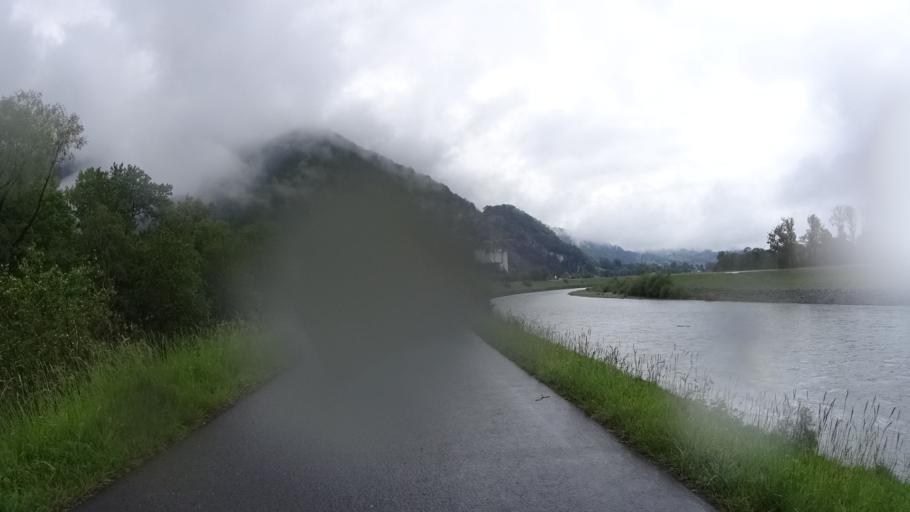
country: LI
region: Balzers
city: Balzers
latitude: 47.0592
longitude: 9.4717
